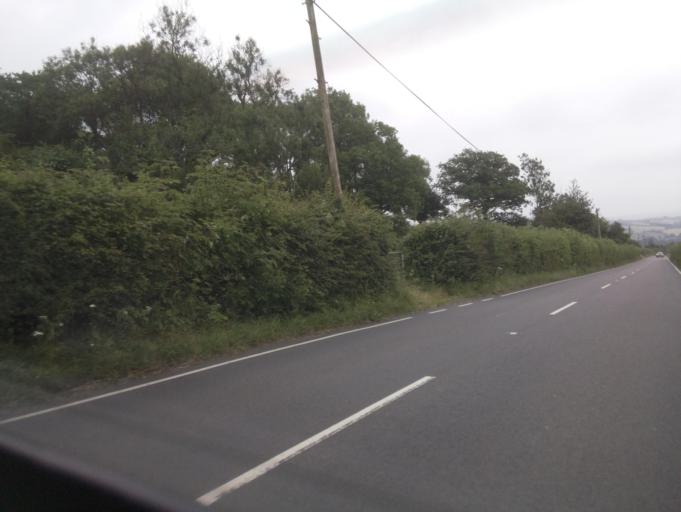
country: GB
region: England
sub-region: Dorset
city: Beaminster
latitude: 50.8229
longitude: -2.7538
